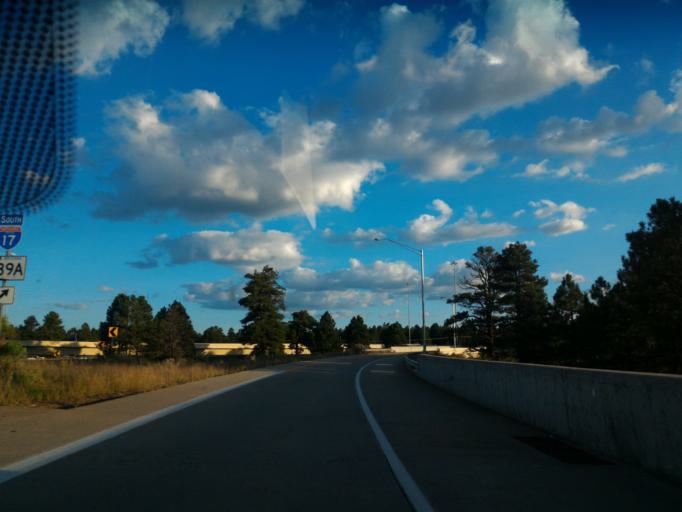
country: US
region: Arizona
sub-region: Coconino County
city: Flagstaff
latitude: 35.1713
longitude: -111.6657
